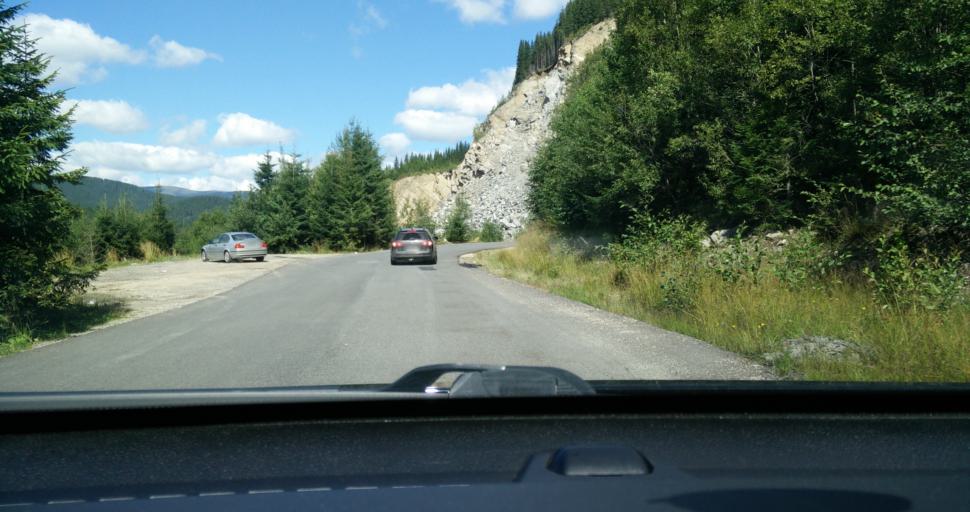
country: RO
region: Alba
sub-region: Comuna Sugag
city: Sugag
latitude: 45.5487
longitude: 23.6317
